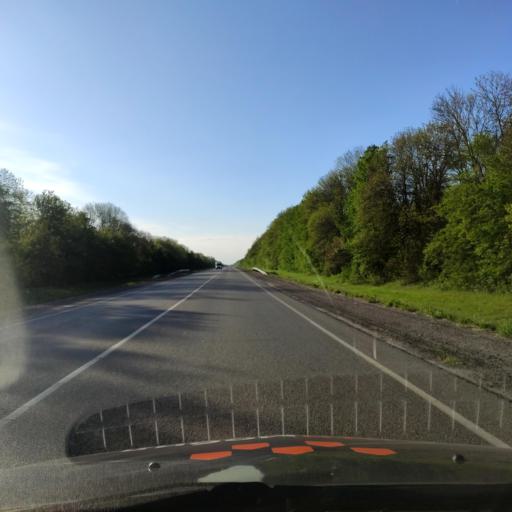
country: RU
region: Lipetsk
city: Yelets
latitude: 52.5763
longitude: 38.6464
